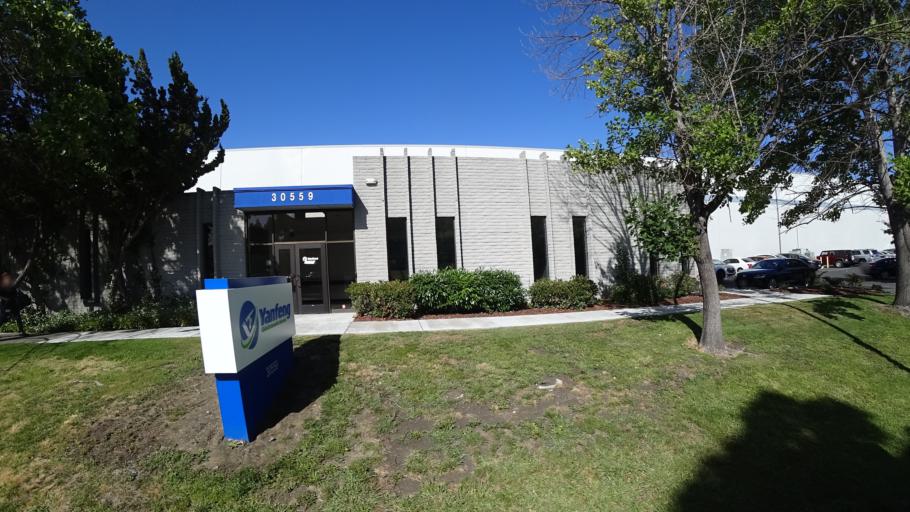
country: US
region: California
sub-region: Alameda County
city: Union City
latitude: 37.6184
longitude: -122.0499
